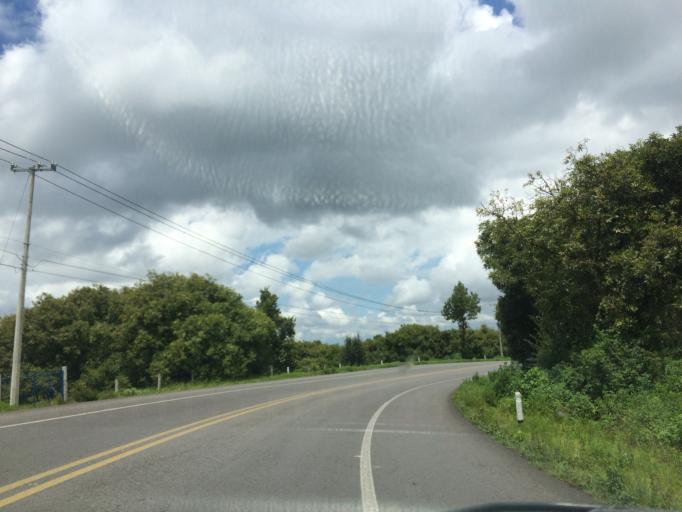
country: MX
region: Michoacan
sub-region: Uruapan
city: Santa Ana Zirosto
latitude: 19.5516
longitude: -102.3022
